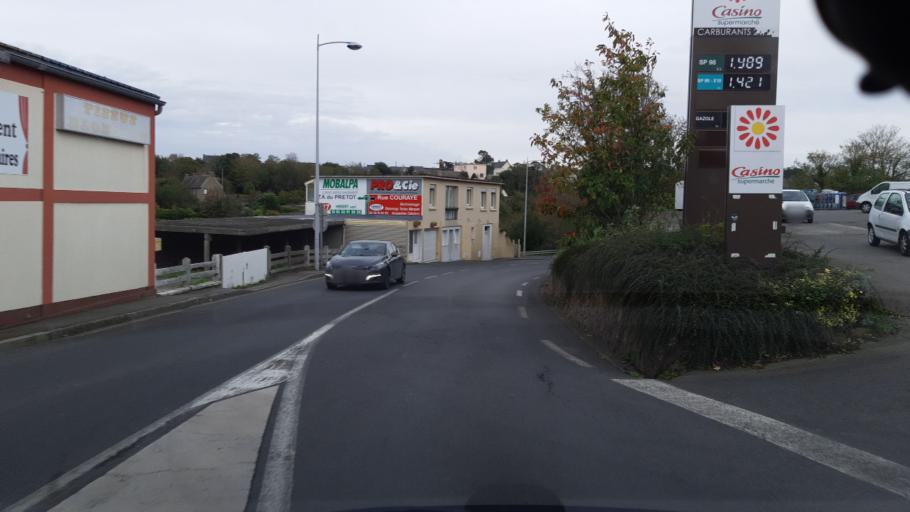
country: FR
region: Lower Normandy
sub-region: Departement de la Manche
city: Donville-les-Bains
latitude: 48.8447
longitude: -1.5836
